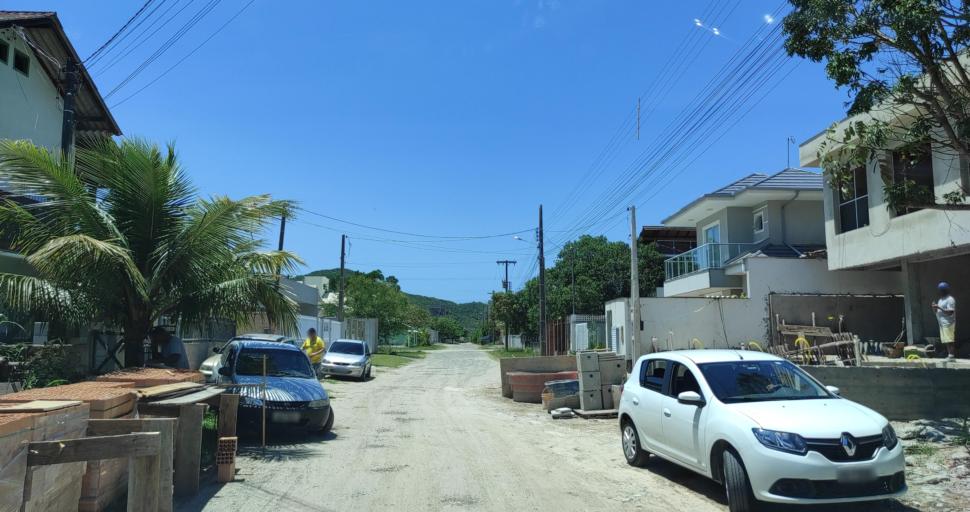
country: BR
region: Santa Catarina
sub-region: Porto Belo
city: Porto Belo
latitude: -27.1746
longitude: -48.5039
